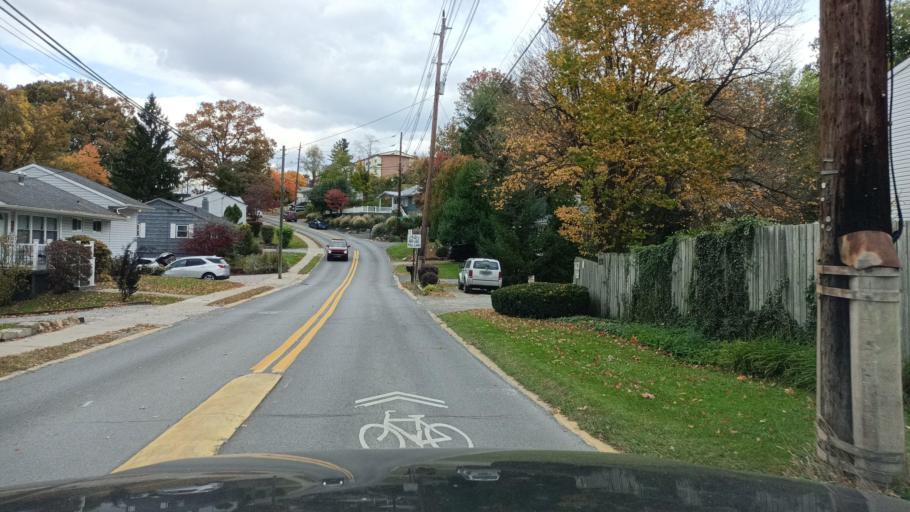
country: US
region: West Virginia
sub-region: Monongalia County
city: Morgantown
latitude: 39.6473
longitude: -79.9528
